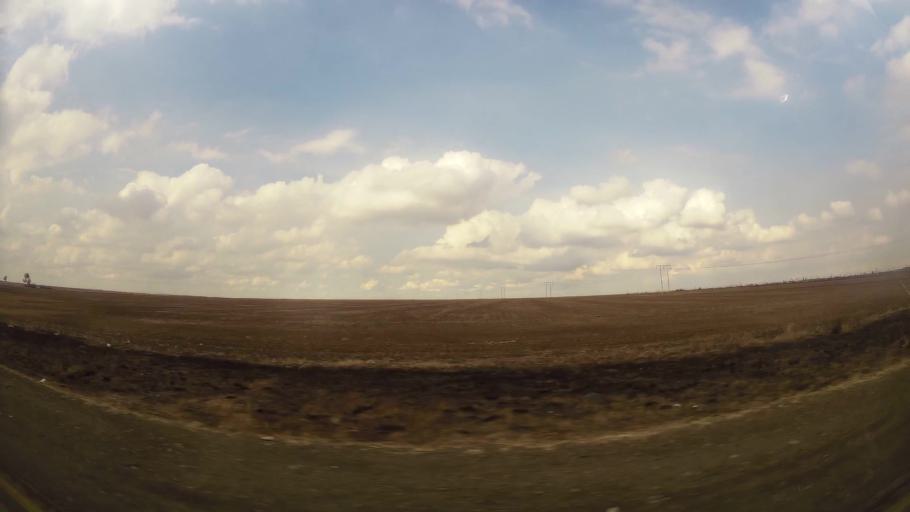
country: ZA
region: Orange Free State
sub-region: Fezile Dabi District Municipality
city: Sasolburg
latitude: -26.8443
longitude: 27.8910
